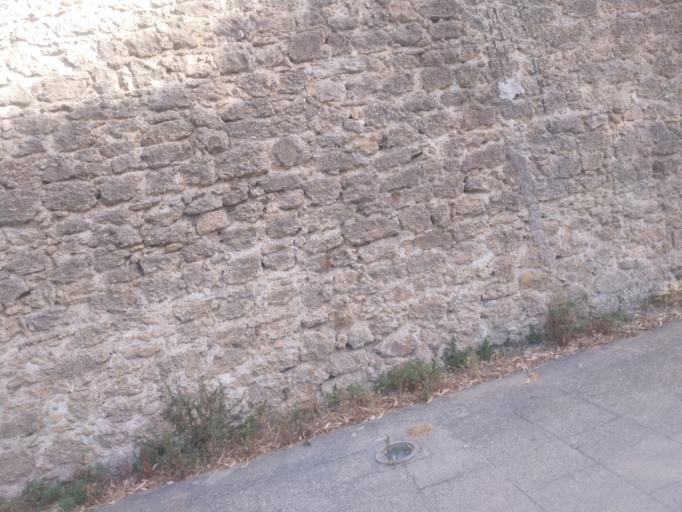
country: ES
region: Andalusia
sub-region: Provincia de Cadiz
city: Cadiz
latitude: 36.5267
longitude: -6.2866
